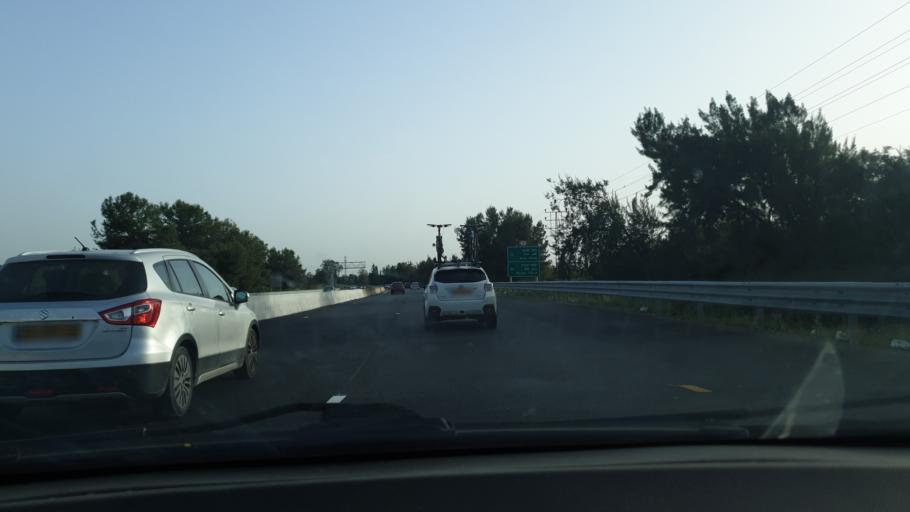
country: IL
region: Central District
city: Tel Mond
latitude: 32.2292
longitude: 34.8835
